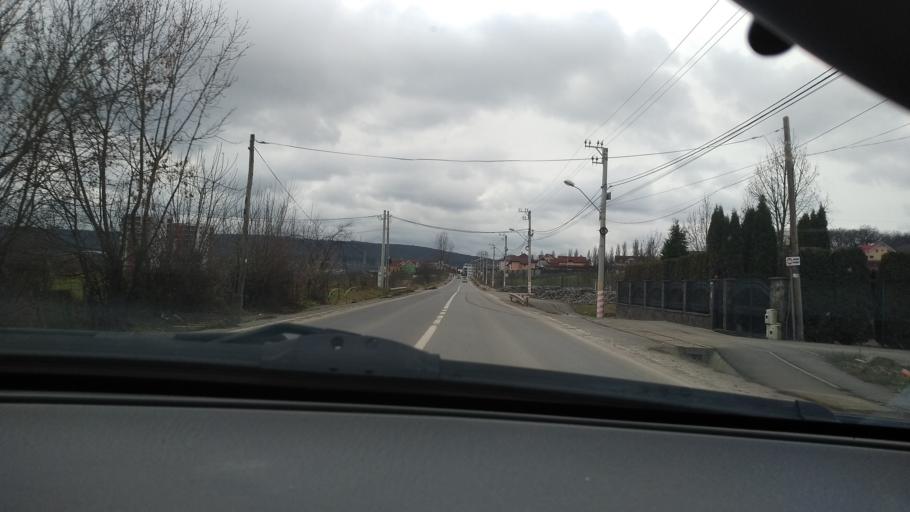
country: RO
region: Mures
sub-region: Comuna Corunca
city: Corunca
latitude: 46.5398
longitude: 24.6064
